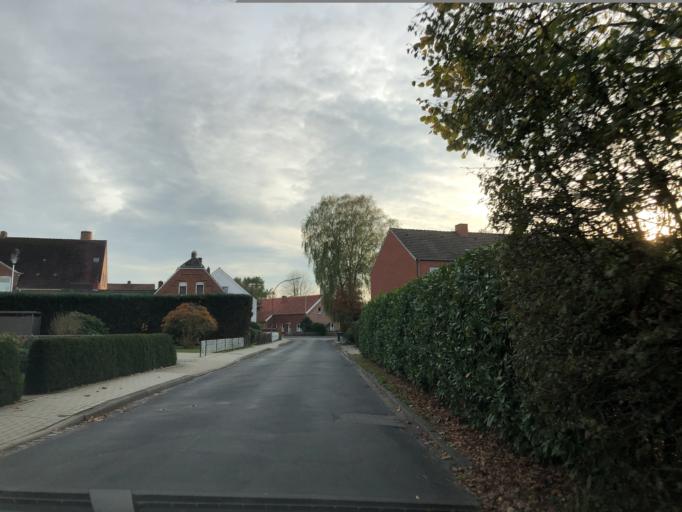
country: DE
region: Lower Saxony
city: Lehe
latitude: 53.0489
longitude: 7.3325
